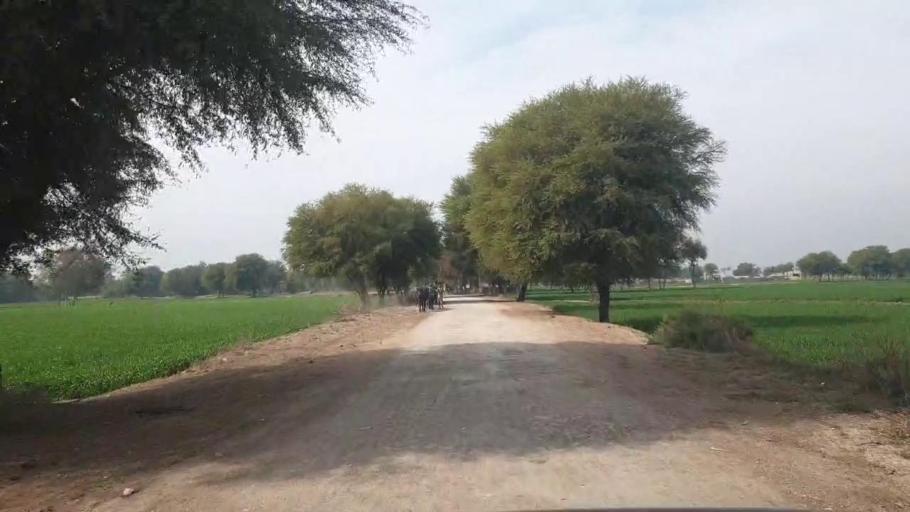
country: PK
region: Sindh
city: Nawabshah
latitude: 26.1192
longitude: 68.4776
